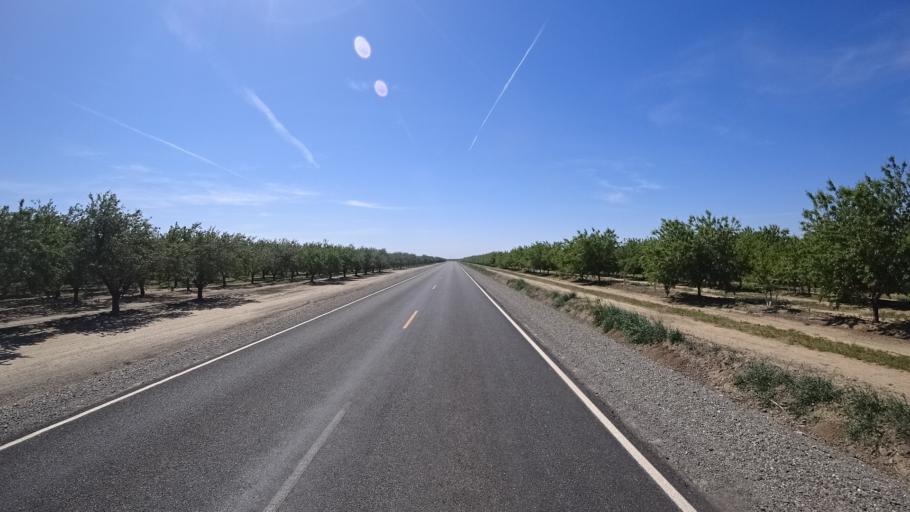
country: US
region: California
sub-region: Glenn County
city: Willows
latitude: 39.6304
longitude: -122.1413
